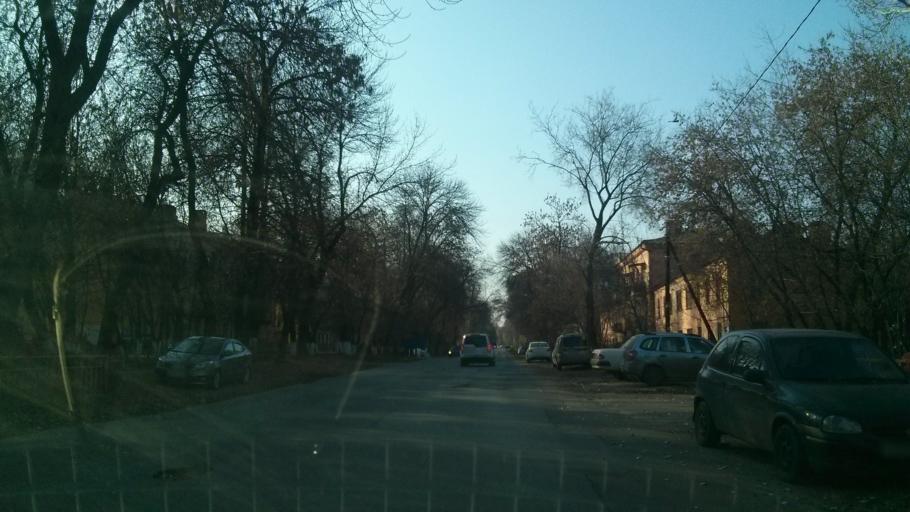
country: RU
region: Nizjnij Novgorod
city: Nizhniy Novgorod
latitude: 56.3135
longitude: 44.0137
